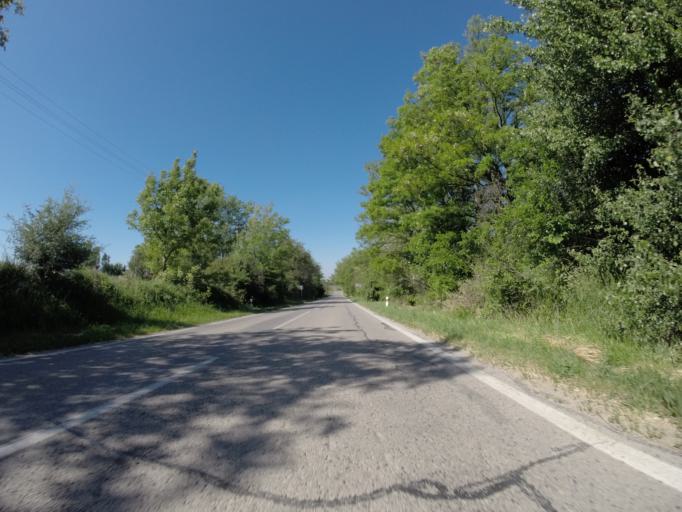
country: SK
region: Trnavsky
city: Hlohovec
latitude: 48.3141
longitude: 17.7711
